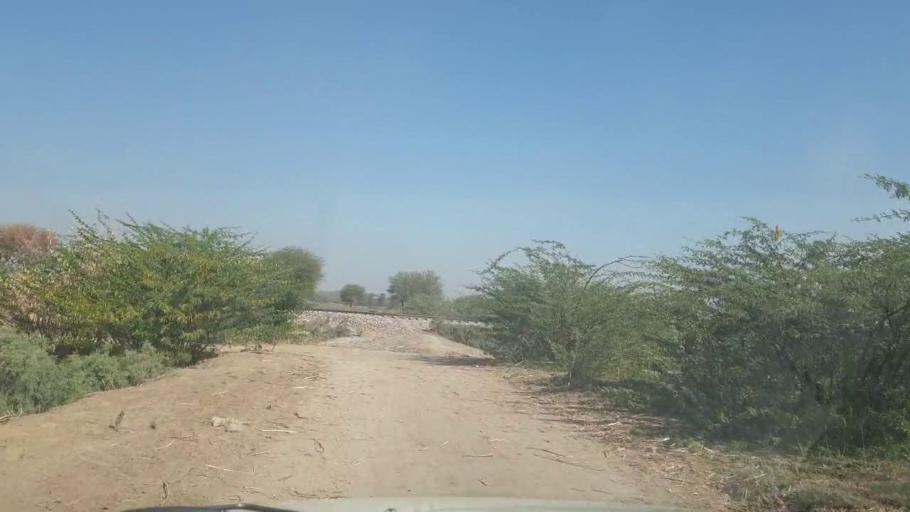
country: PK
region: Sindh
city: Mirpur Khas
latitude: 25.5207
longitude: 69.1617
